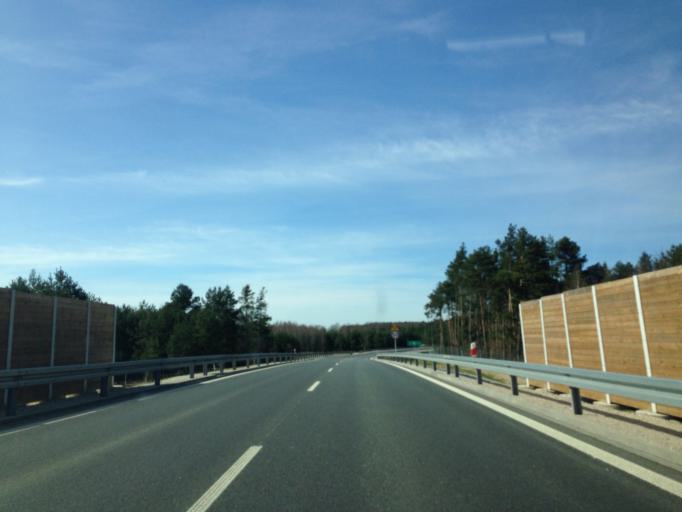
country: PL
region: Lodz Voivodeship
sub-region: Powiat sieradzki
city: Sieradz
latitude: 51.6002
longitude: 18.8152
